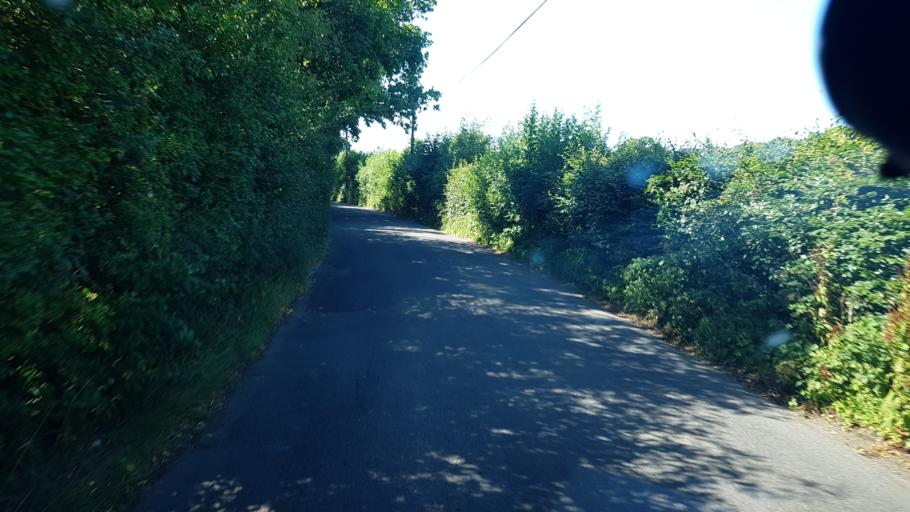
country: GB
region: England
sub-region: Kent
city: Edenbridge
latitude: 51.2246
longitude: 0.0786
